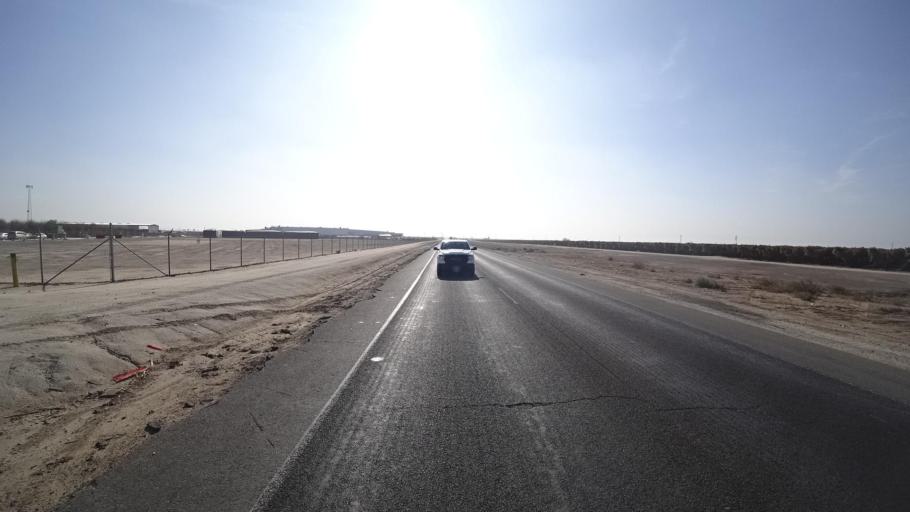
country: US
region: California
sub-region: Kern County
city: McFarland
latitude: 35.7225
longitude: -119.1568
